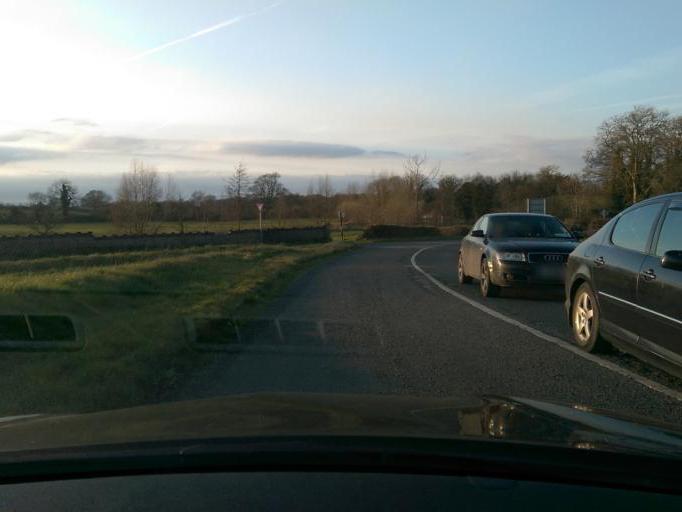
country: IE
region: Munster
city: Nenagh Bridge
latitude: 52.8837
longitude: -8.1959
